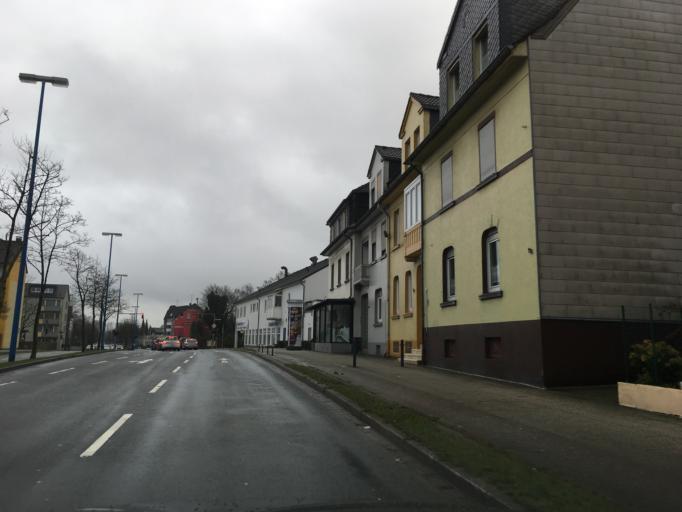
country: DE
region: North Rhine-Westphalia
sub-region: Regierungsbezirk Dusseldorf
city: Velbert
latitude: 51.3325
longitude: 7.0313
